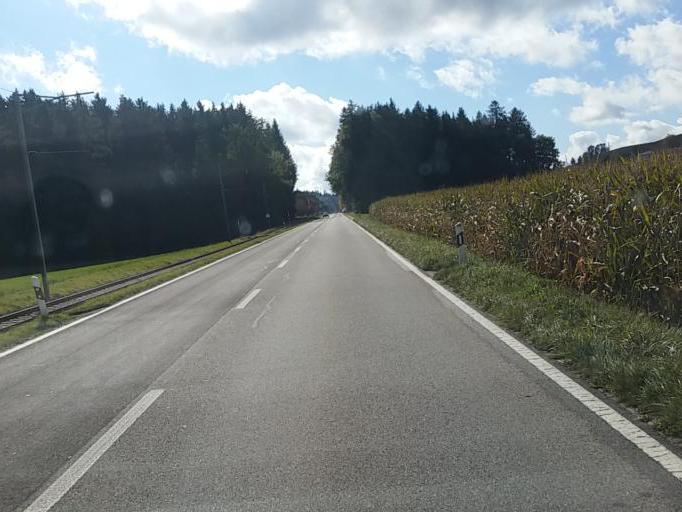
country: CH
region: Bern
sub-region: Emmental District
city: Sumiswald
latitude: 47.0663
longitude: 7.7488
